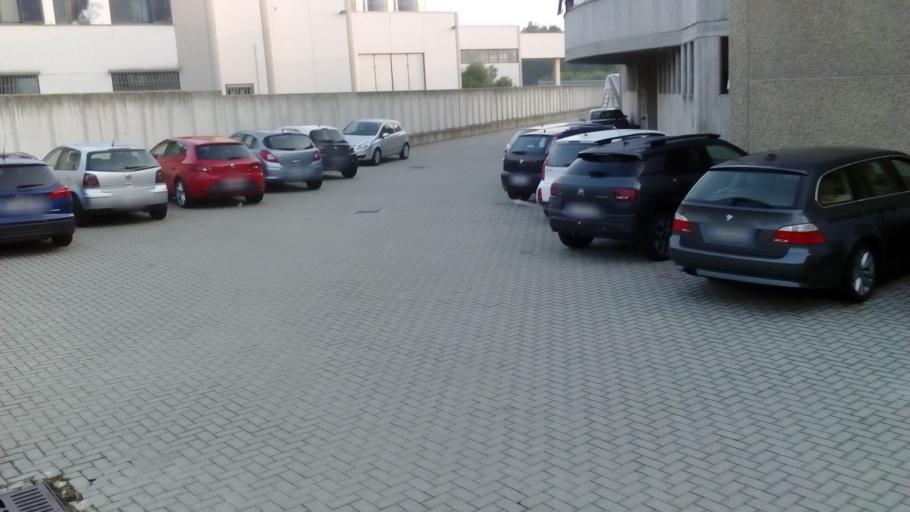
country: IT
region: Piedmont
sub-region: Provincia di Novara
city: Varallo Pombia
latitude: 45.6719
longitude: 8.6177
